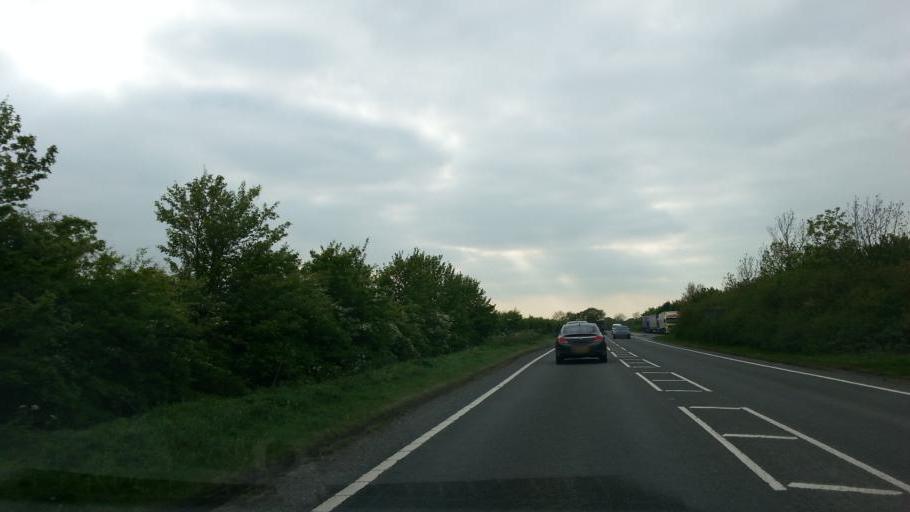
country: GB
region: England
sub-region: Lincolnshire
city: Navenby
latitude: 53.0625
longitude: -0.6035
